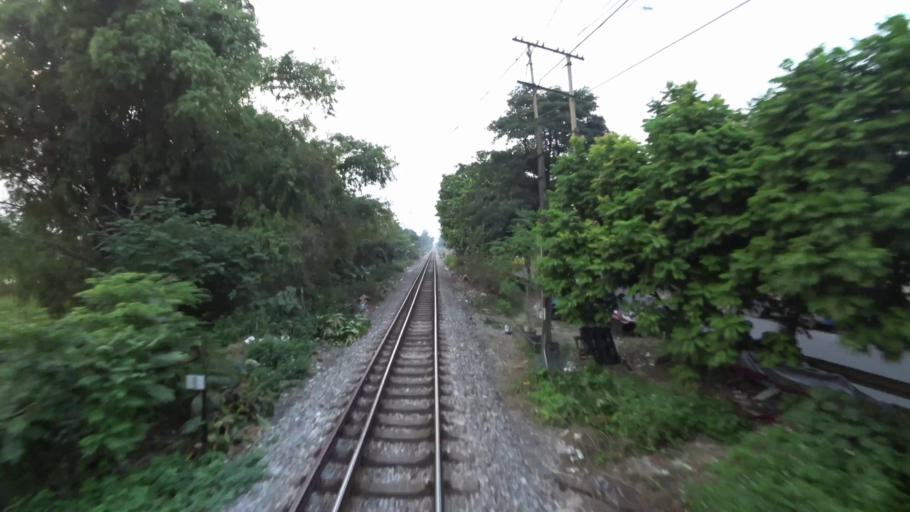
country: VN
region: Ha Noi
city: Dong Anh
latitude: 21.1416
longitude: 105.8649
